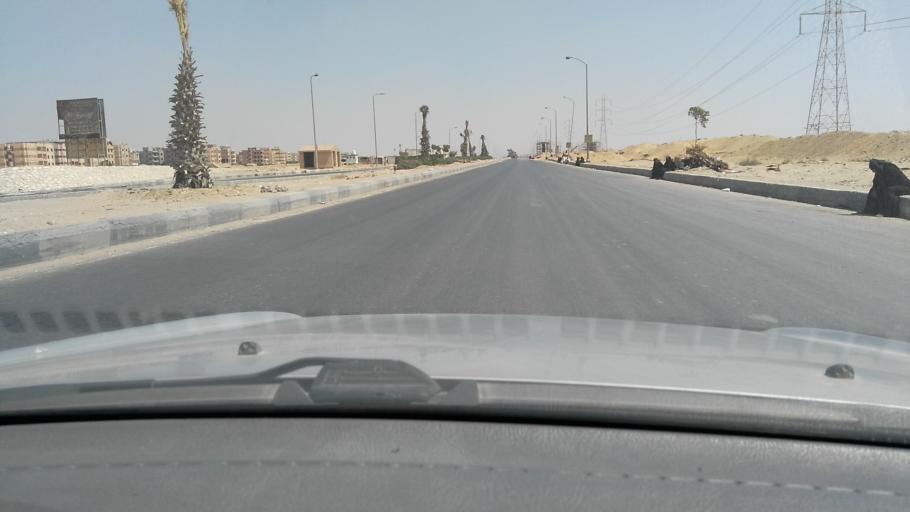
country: EG
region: Al Jizah
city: Madinat Sittah Uktubar
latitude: 29.9308
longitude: 30.9434
